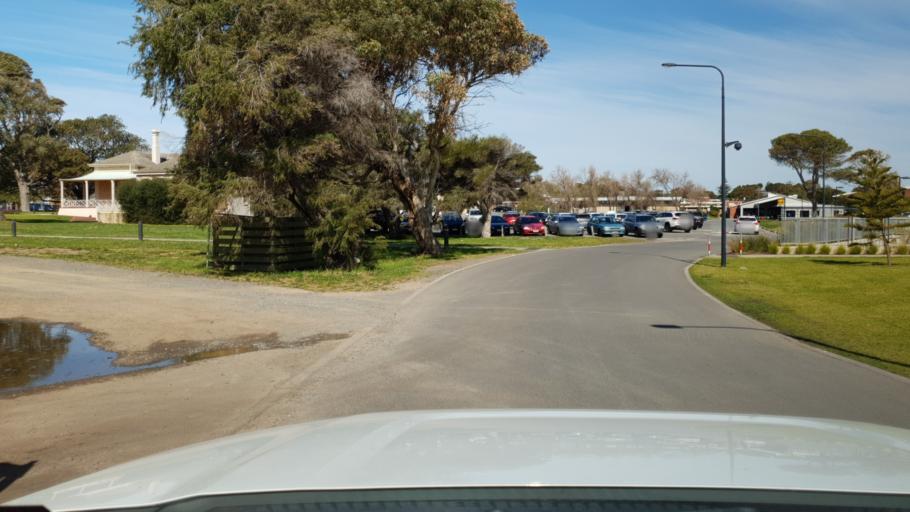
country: AU
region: South Australia
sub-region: Holdfast Bay
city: North Brighton
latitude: -35.0034
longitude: 138.5139
